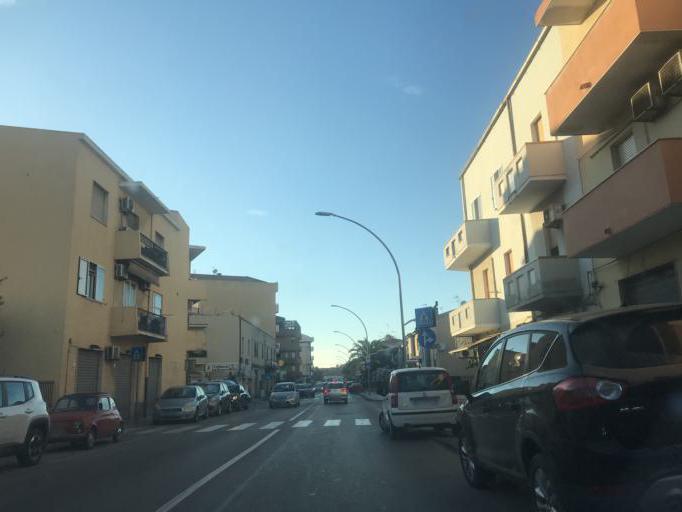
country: IT
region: Sardinia
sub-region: Provincia di Sassari
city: Alghero
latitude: 40.5746
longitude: 8.3216
